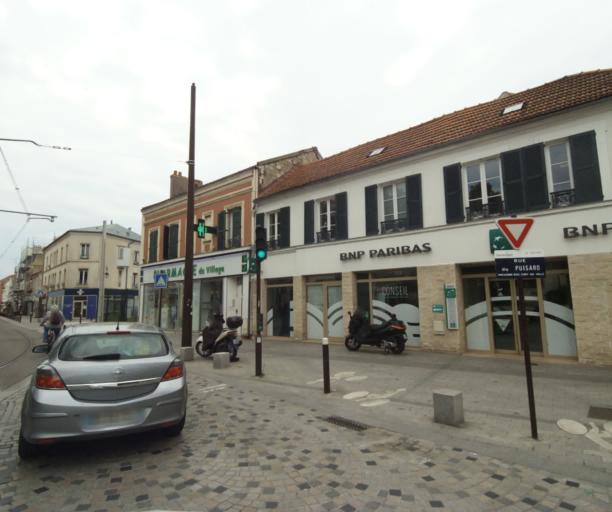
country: FR
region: Ile-de-France
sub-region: Departement des Hauts-de-Seine
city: Gennevilliers
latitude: 48.9328
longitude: 2.2965
